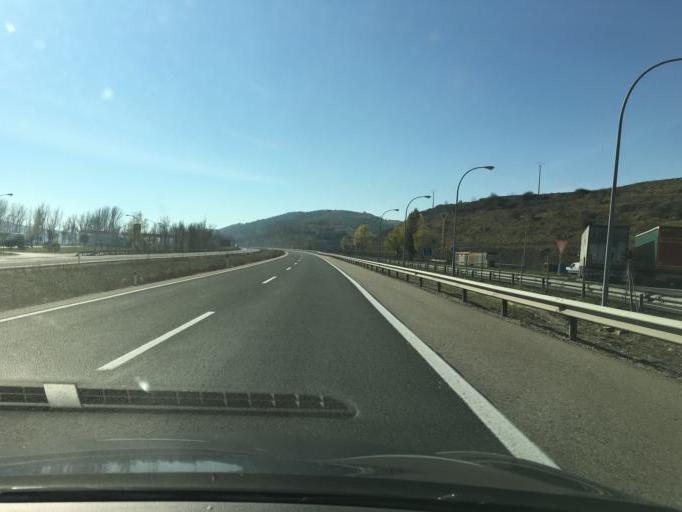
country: ES
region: Castille and Leon
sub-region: Provincia de Burgos
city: Briviesca
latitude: 42.5281
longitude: -3.3325
